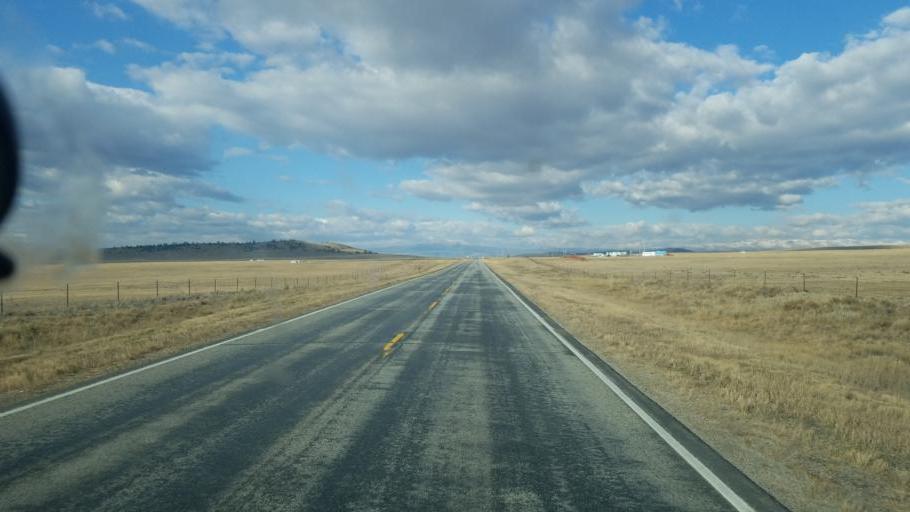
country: US
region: Colorado
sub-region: Park County
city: Fairplay
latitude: 39.0425
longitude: -105.7070
